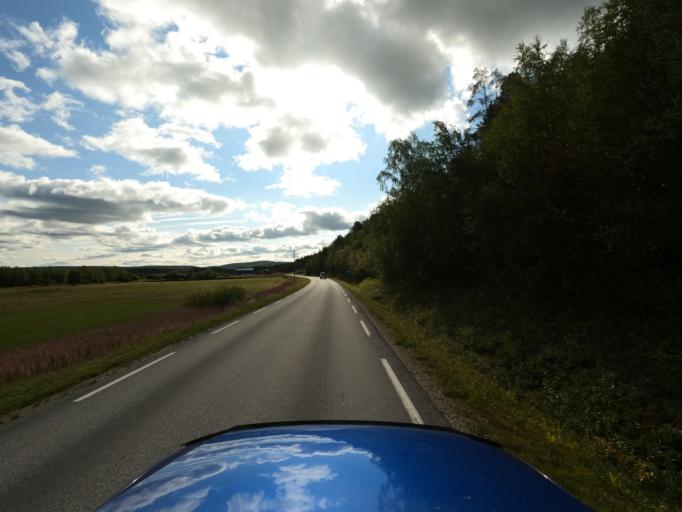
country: NO
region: Finnmark Fylke
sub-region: Karasjok
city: Karasjohka
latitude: 69.4091
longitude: 25.8062
